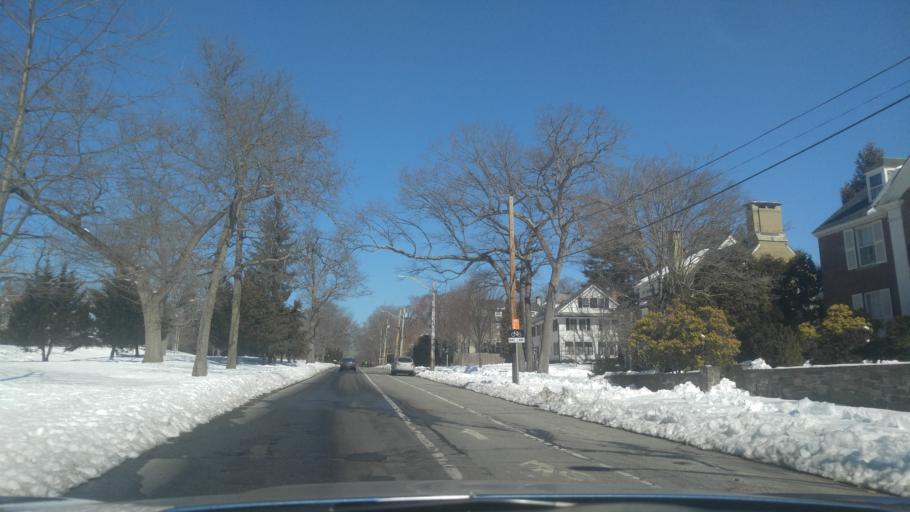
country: US
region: Rhode Island
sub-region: Providence County
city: East Providence
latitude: 41.8366
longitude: -71.3846
